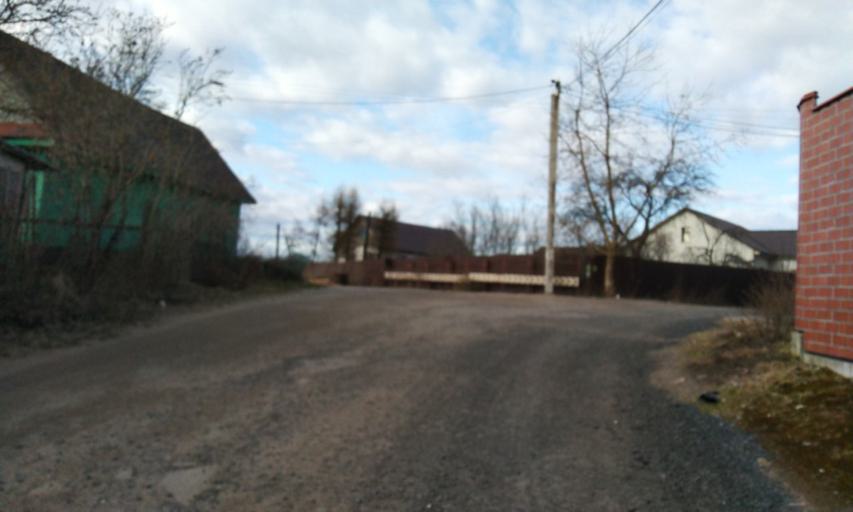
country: RU
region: Leningrad
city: Toksovo
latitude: 60.1232
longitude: 30.4868
